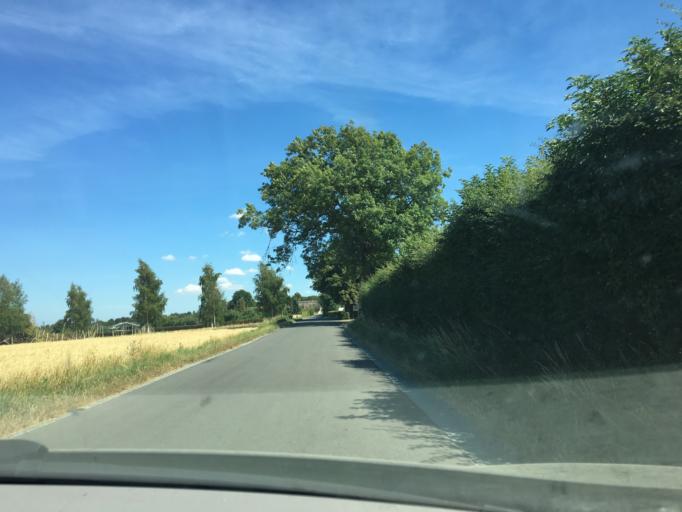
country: DK
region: South Denmark
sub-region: Middelfart Kommune
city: Norre Aby
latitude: 55.5063
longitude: 9.8857
